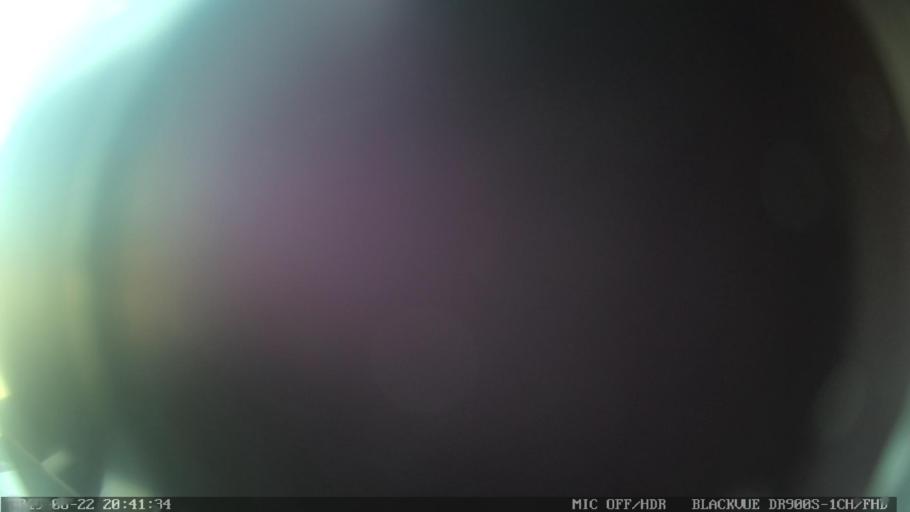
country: PT
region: Castelo Branco
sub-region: Proenca-A-Nova
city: Proenca-a-Nova
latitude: 39.6866
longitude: -7.8066
